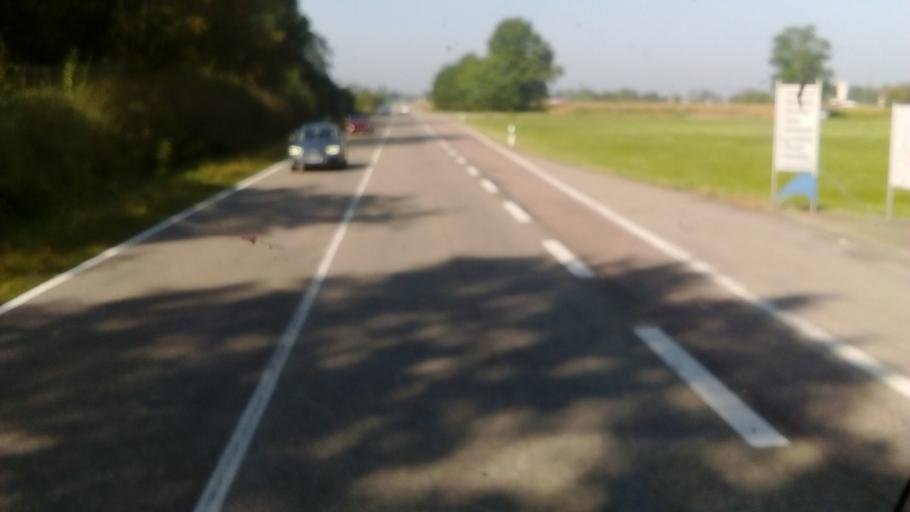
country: DE
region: Baden-Wuerttemberg
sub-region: Freiburg Region
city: Rheinau
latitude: 48.6580
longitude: 7.9530
